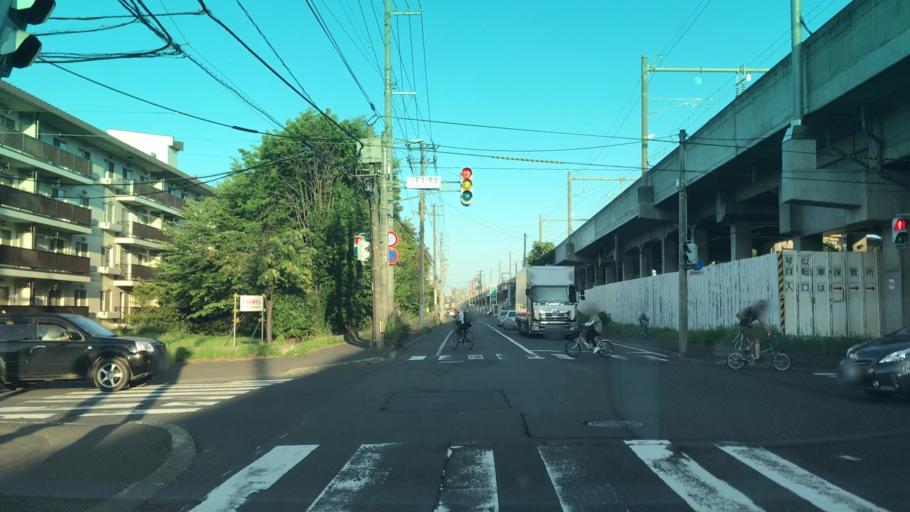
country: JP
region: Hokkaido
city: Sapporo
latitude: 43.0802
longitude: 141.3104
